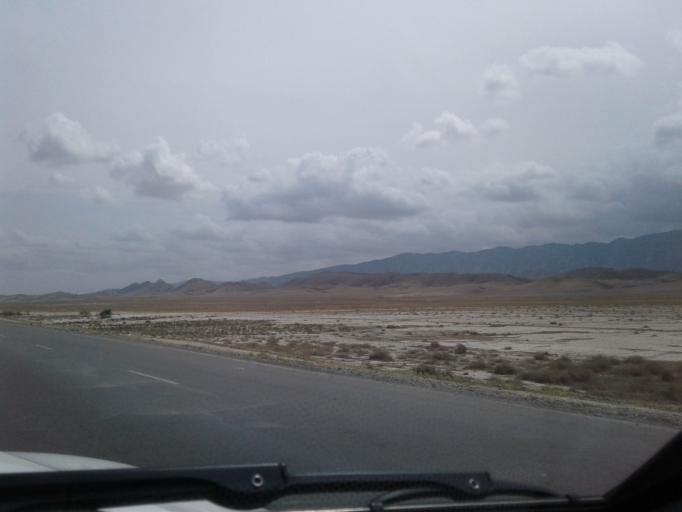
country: IR
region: Razavi Khorasan
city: Dargaz
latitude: 37.7135
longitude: 59.0215
